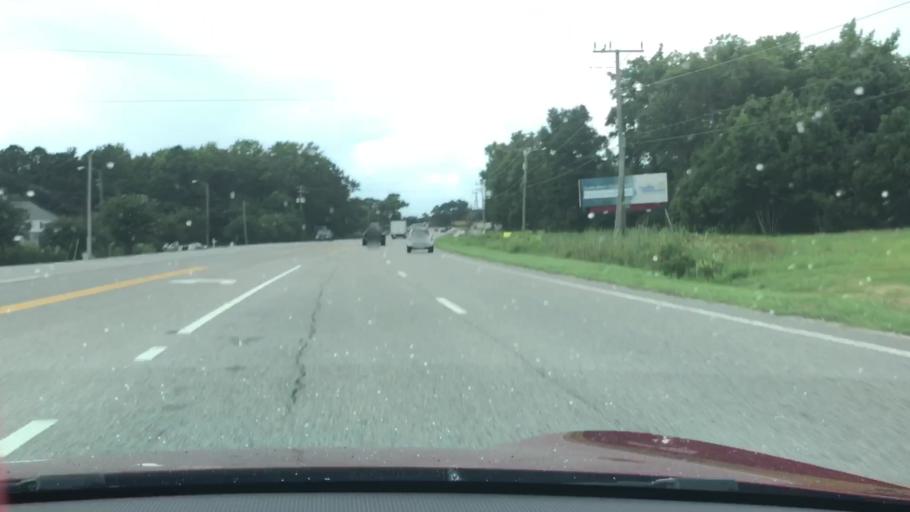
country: US
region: North Carolina
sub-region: Dare County
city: Southern Shores
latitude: 36.0963
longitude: -75.8118
